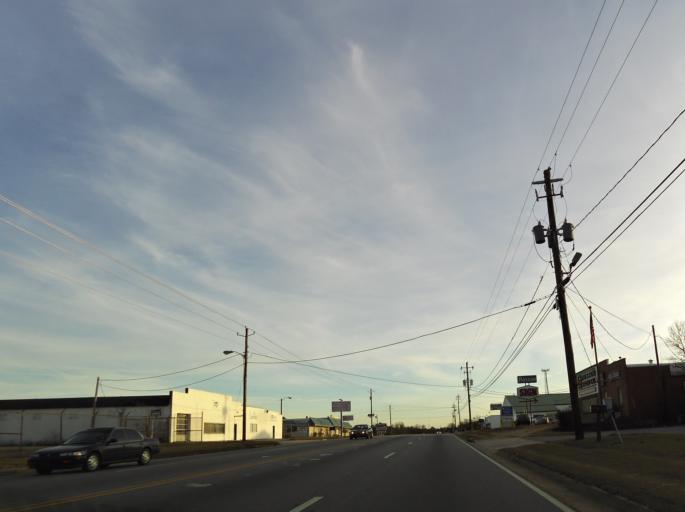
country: US
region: Georgia
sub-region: Bibb County
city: Macon
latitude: 32.8066
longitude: -83.6405
